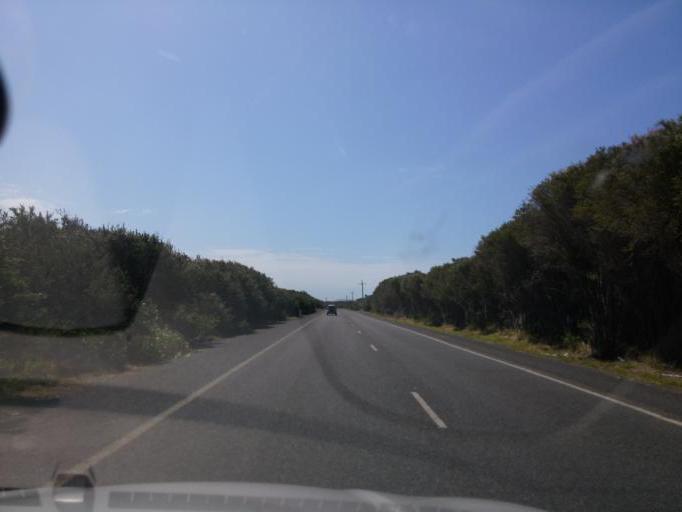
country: AU
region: New South Wales
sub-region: Great Lakes
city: Forster
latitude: -32.2794
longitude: 152.5244
